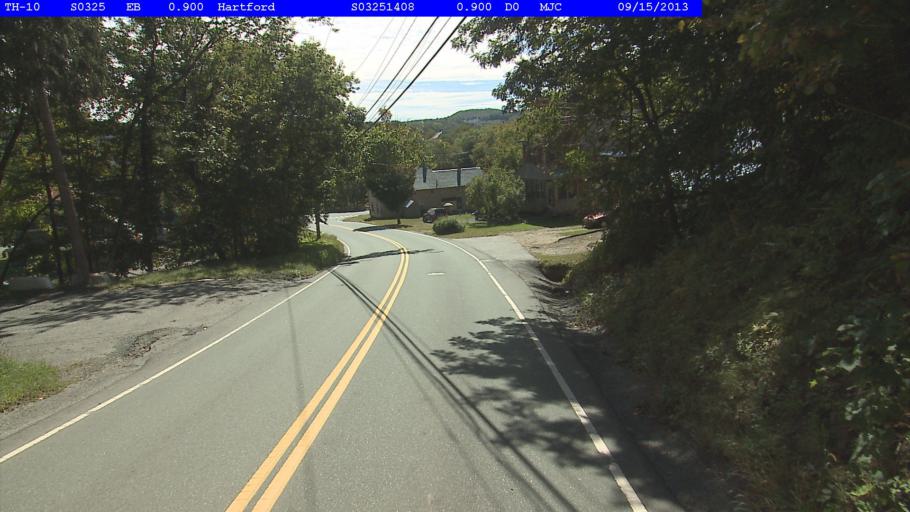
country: US
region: Vermont
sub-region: Windsor County
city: White River Junction
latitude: 43.6420
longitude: -72.3208
